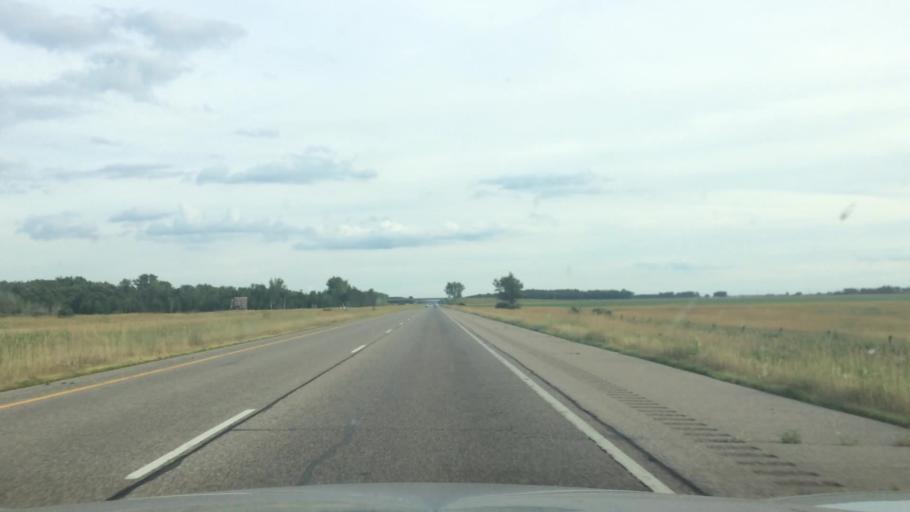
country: US
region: Wisconsin
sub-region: Waushara County
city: Wautoma
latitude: 44.1636
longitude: -89.5327
